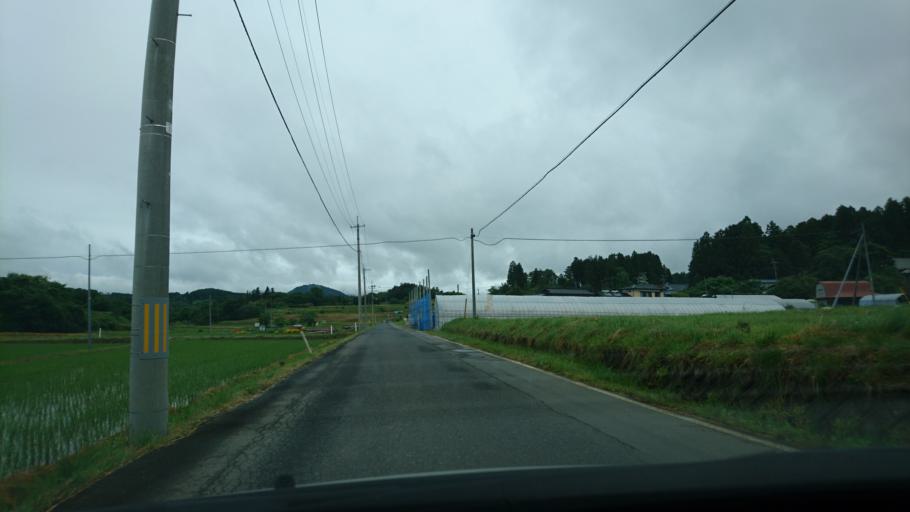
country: JP
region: Iwate
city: Ichinoseki
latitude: 38.9232
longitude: 141.2093
